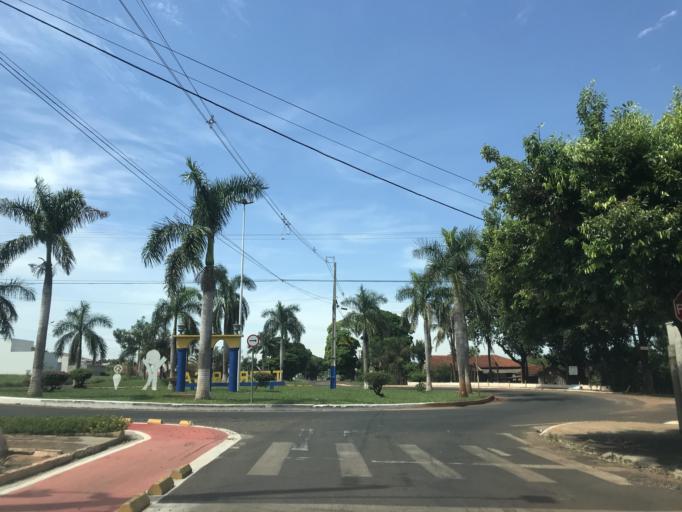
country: BR
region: Parana
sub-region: Terra Rica
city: Terra Rica
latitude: -22.7341
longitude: -52.6246
